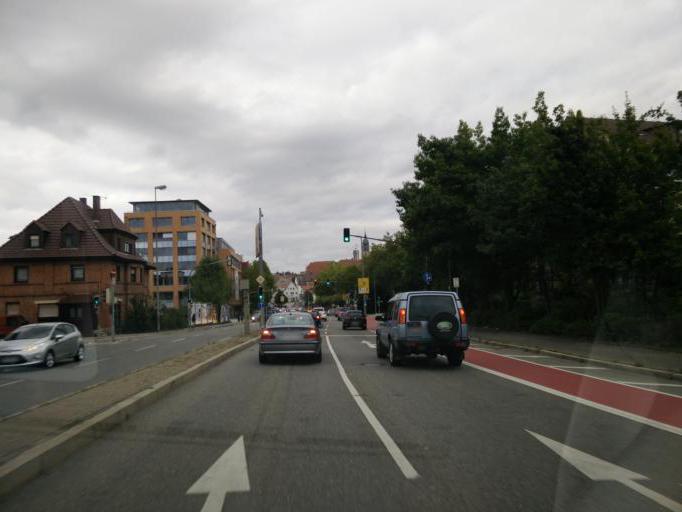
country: DE
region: Baden-Wuerttemberg
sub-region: Regierungsbezirk Stuttgart
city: Boeblingen
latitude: 48.6843
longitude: 9.0060
